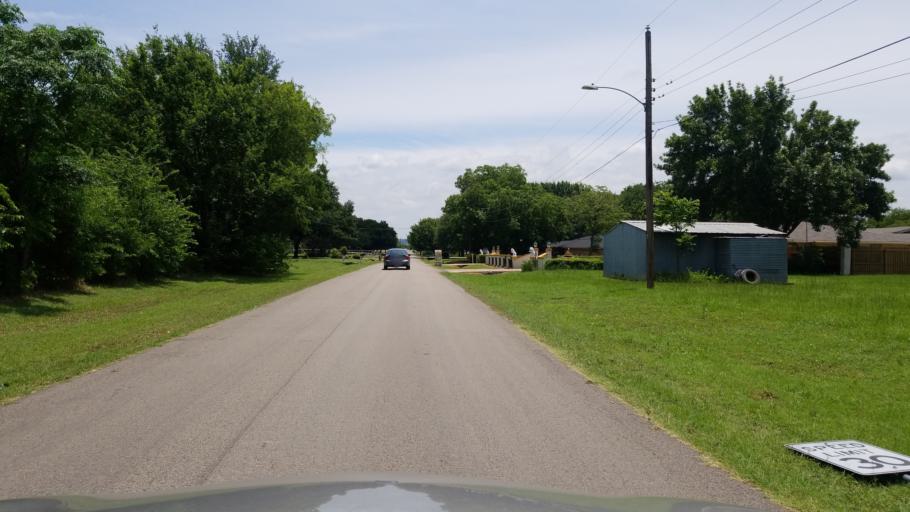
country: US
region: Texas
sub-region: Dallas County
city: Grand Prairie
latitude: 32.6739
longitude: -97.0304
